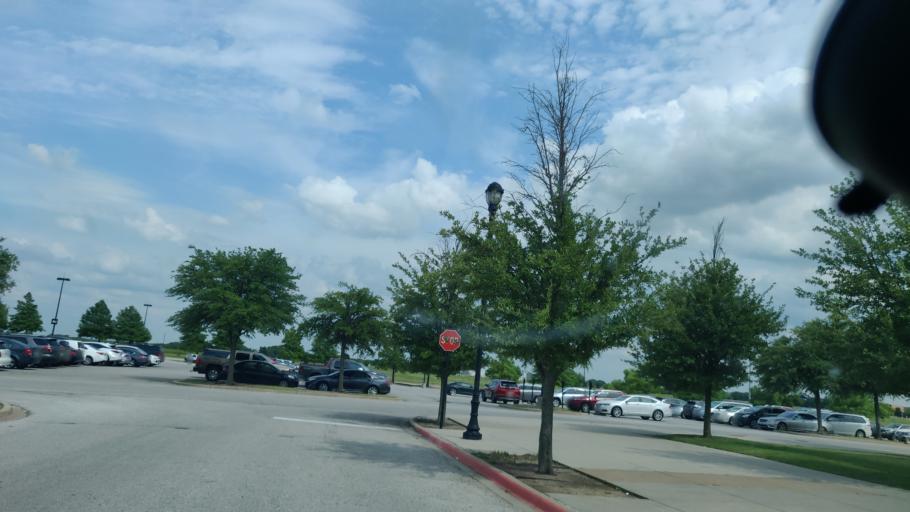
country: US
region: Texas
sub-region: Dallas County
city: Sachse
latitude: 32.9507
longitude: -96.6133
